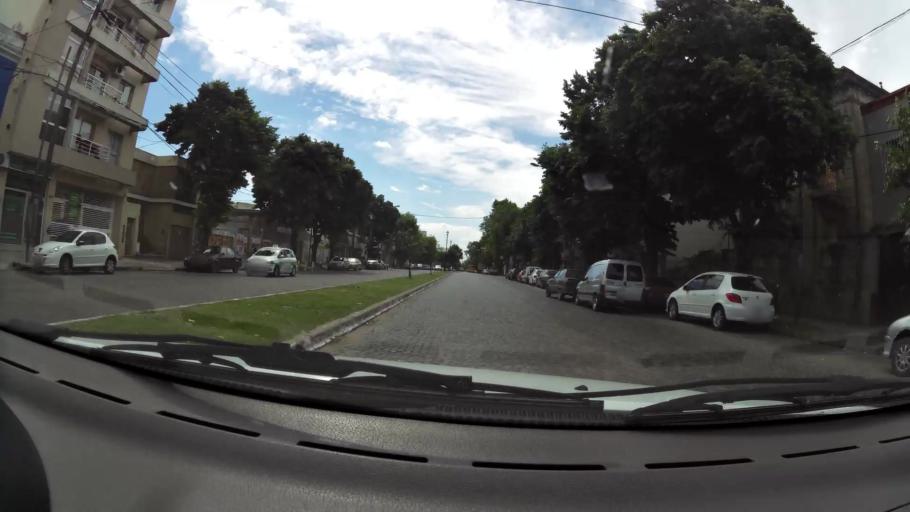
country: AR
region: Buenos Aires
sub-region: Partido de La Plata
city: La Plata
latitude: -34.9298
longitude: -57.9297
